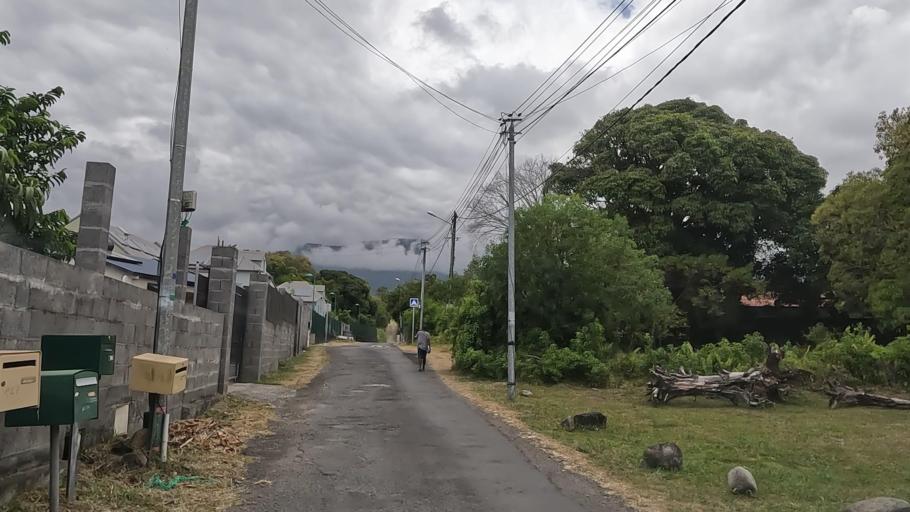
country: RE
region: Reunion
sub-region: Reunion
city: Saint-Benoit
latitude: -21.0919
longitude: 55.7449
